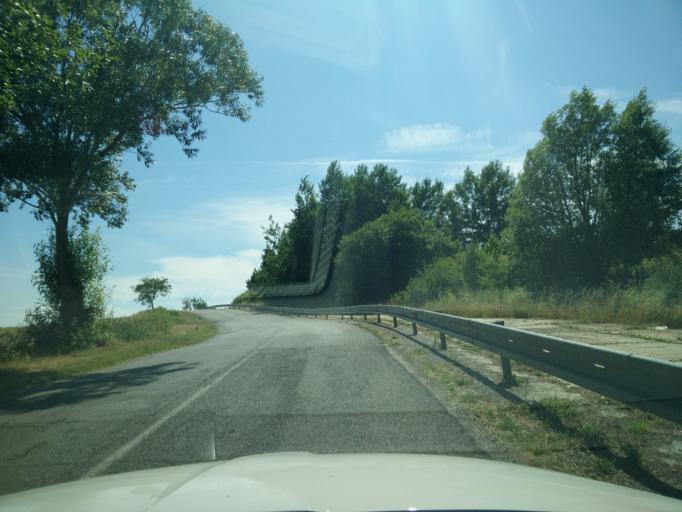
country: SK
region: Nitriansky
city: Bojnice
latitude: 48.8624
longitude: 18.6255
